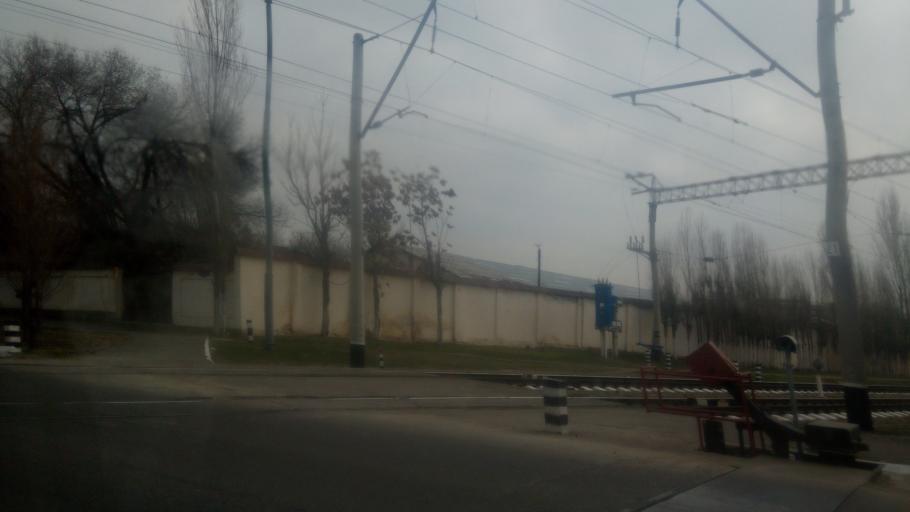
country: UZ
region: Toshkent
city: Salor
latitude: 41.3361
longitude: 69.3202
